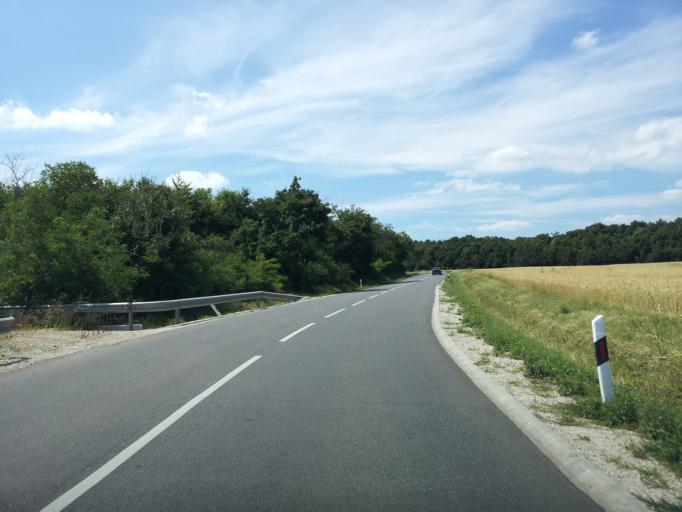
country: HU
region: Veszprem
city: Liter
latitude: 47.1092
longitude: 18.0065
